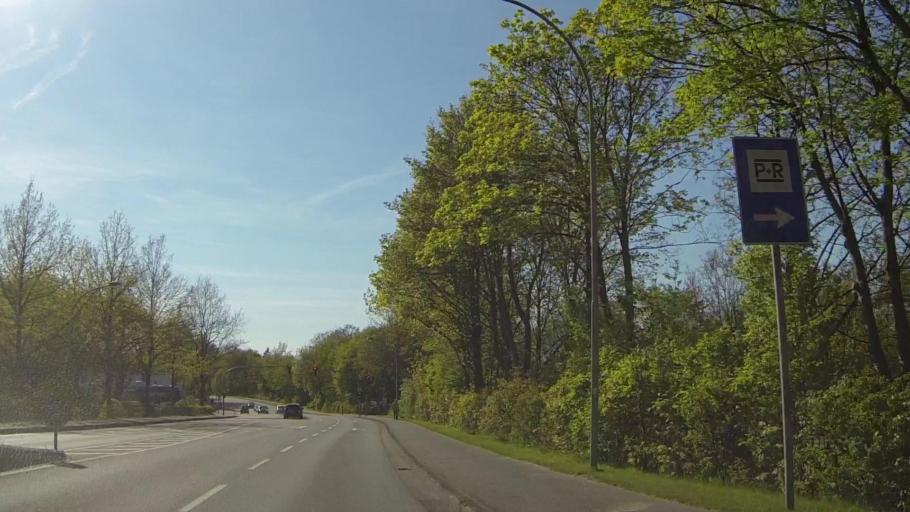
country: DE
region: Schleswig-Holstein
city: Rellingen
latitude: 53.6446
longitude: 9.8111
